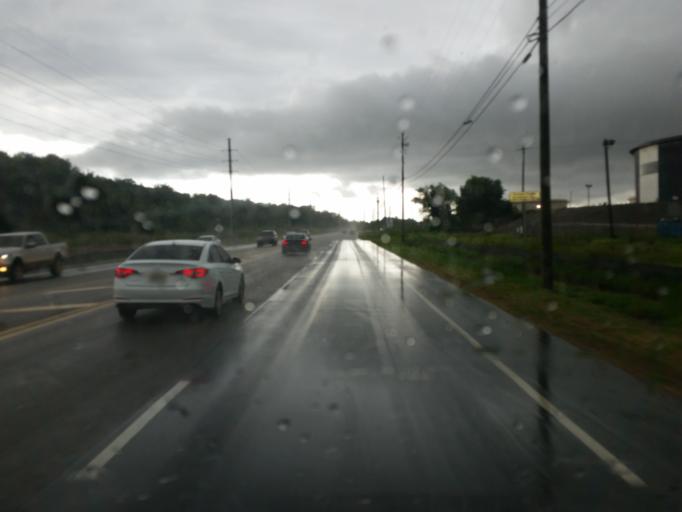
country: US
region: Alabama
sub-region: Mobile County
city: Mobile
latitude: 30.7194
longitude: -88.0355
